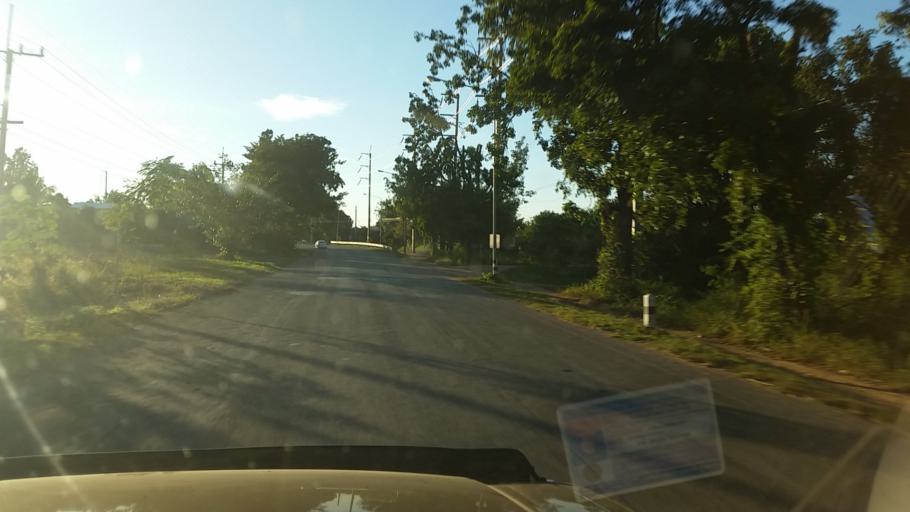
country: TH
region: Chaiyaphum
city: Sap Yai
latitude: 15.6588
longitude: 101.6482
